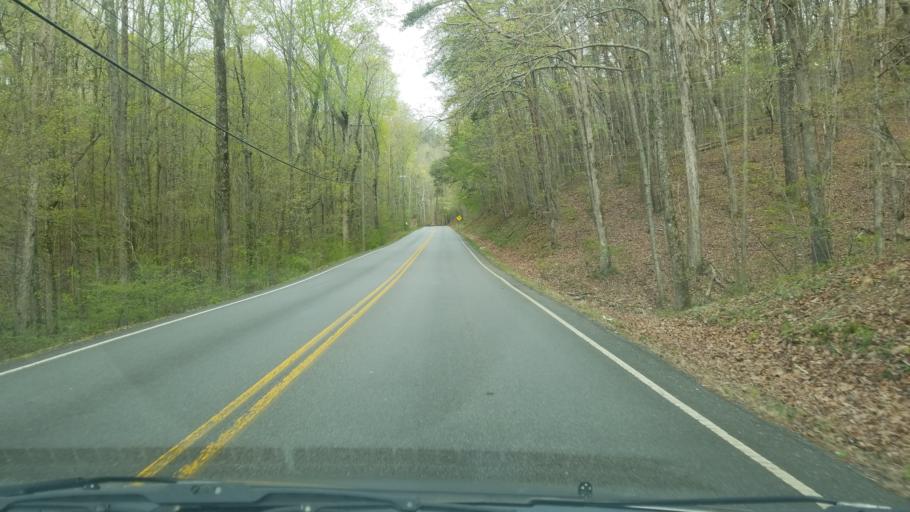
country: US
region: Tennessee
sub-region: Hamilton County
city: Collegedale
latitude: 35.0265
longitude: -85.0663
